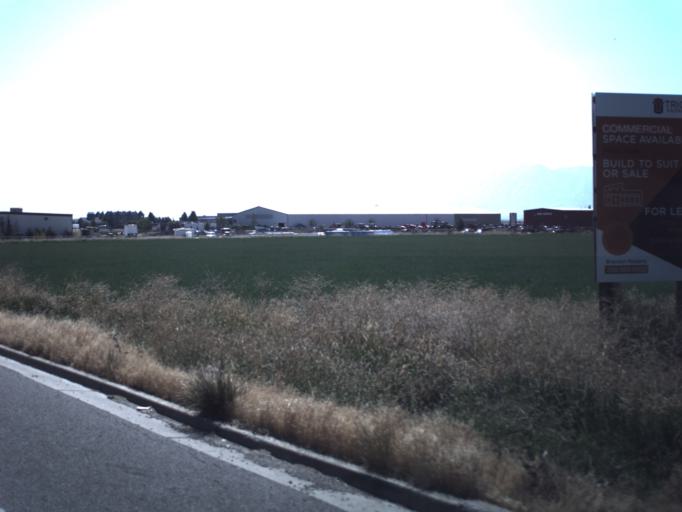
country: US
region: Utah
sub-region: Cache County
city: Hyde Park
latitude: 41.8082
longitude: -111.8334
